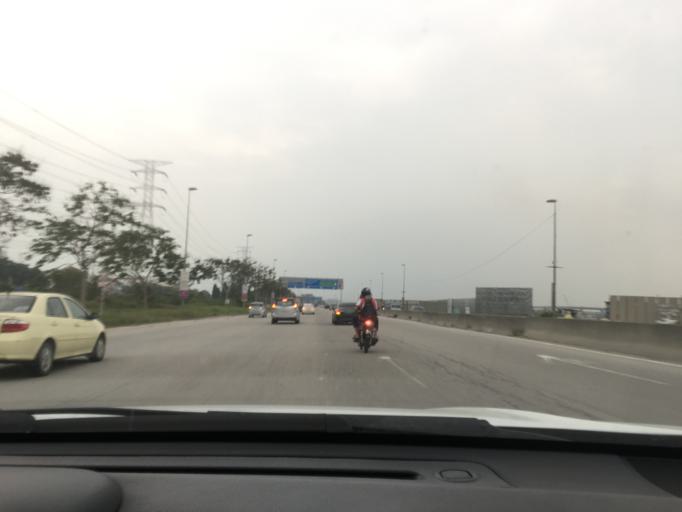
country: MY
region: Selangor
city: Klang
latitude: 3.0999
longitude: 101.4428
